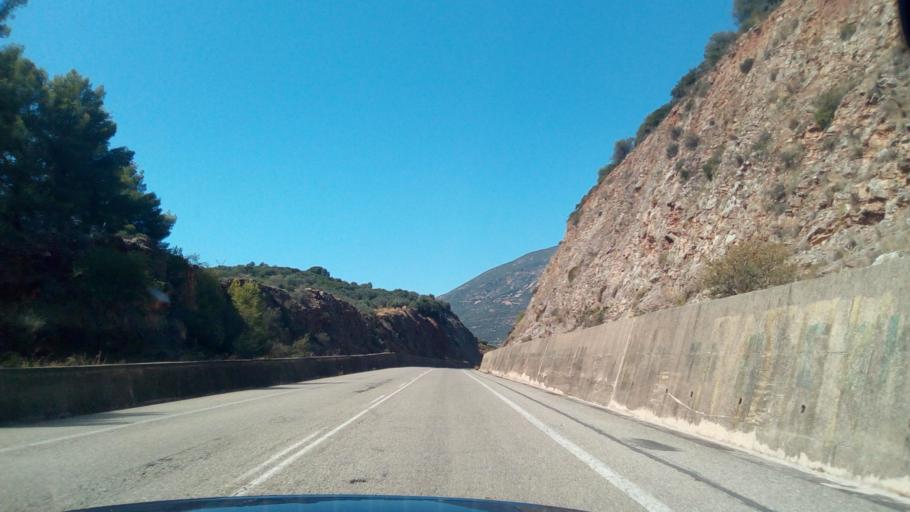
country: GR
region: West Greece
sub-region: Nomos Achaias
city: Selianitika
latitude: 38.3881
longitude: 22.0791
